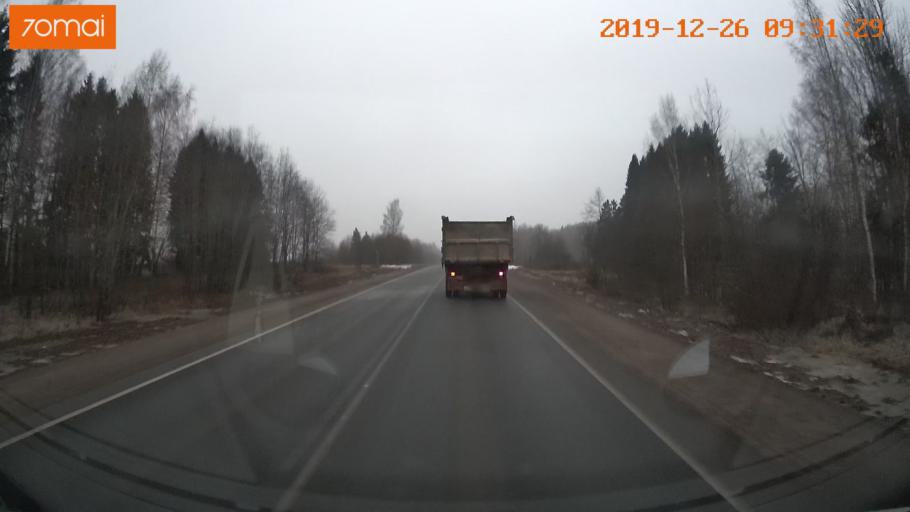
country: RU
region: Vologda
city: Gryazovets
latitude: 59.0696
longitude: 40.1273
